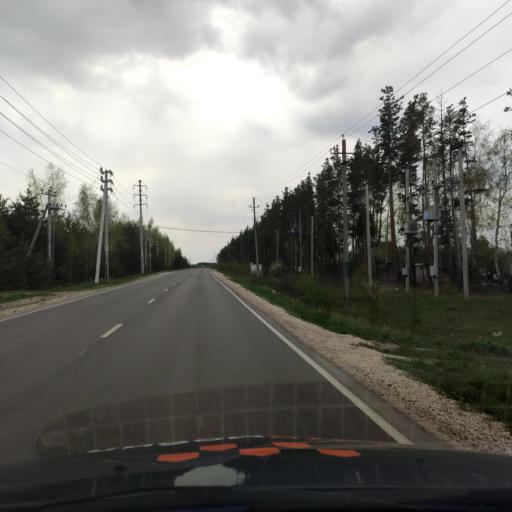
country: RU
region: Voronezj
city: Podgornoye
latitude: 51.8627
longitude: 39.1676
